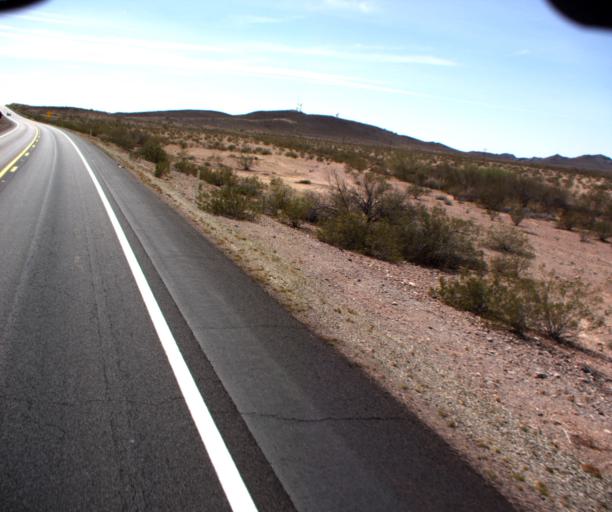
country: US
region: Arizona
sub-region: La Paz County
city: Quartzsite
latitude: 33.2535
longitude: -114.2465
